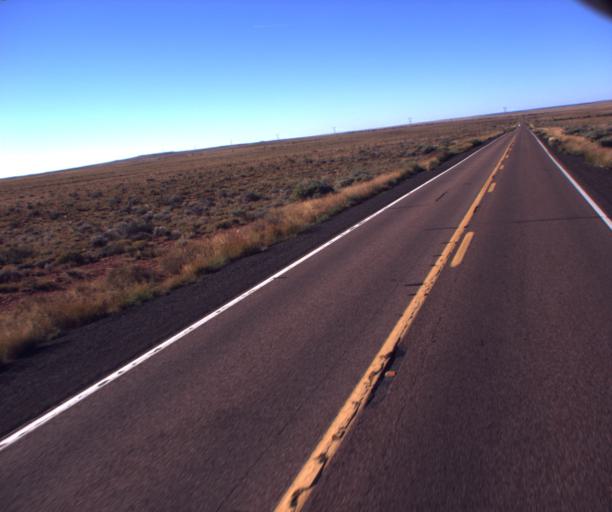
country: US
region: Arizona
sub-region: Navajo County
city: Holbrook
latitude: 34.8127
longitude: -110.2013
